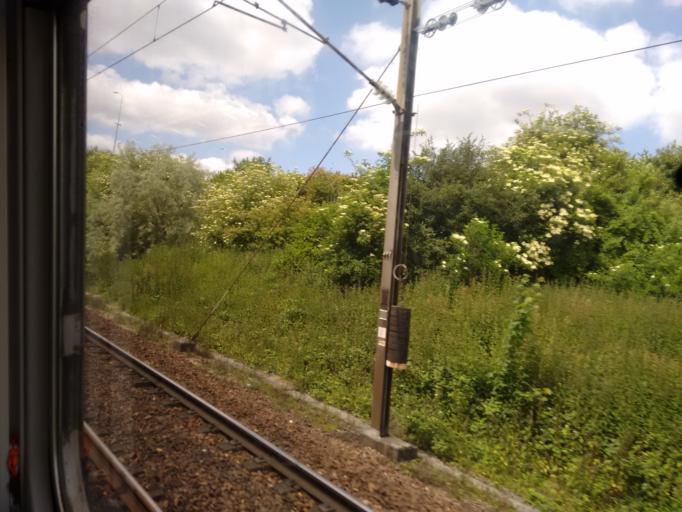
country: FR
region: Ile-de-France
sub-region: Departement du Val-d'Oise
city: Roissy-en-France
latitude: 49.0062
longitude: 2.5311
